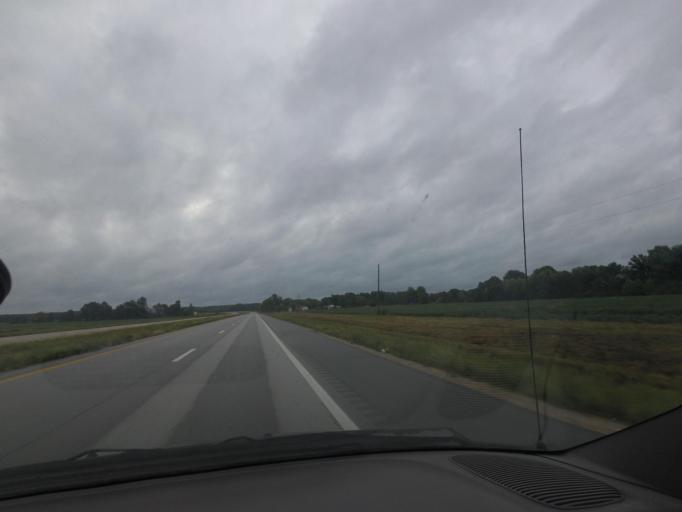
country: US
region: Missouri
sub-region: Shelby County
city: Shelbina
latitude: 39.6666
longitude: -91.9166
